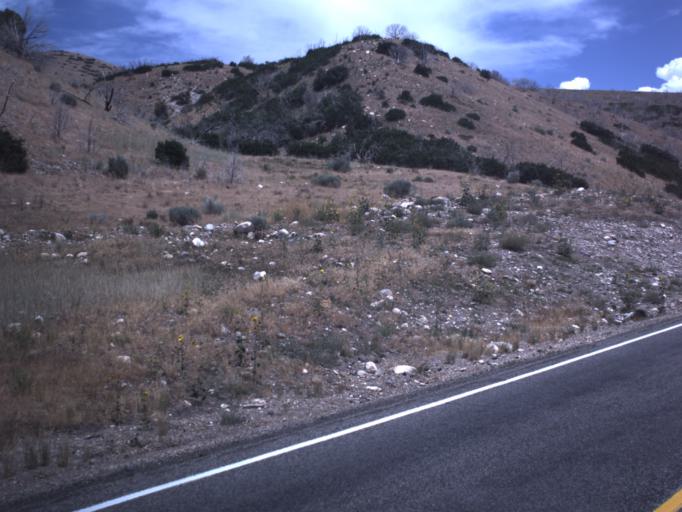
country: US
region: Utah
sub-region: Sanpete County
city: Fountain Green
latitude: 39.7029
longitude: -111.7040
